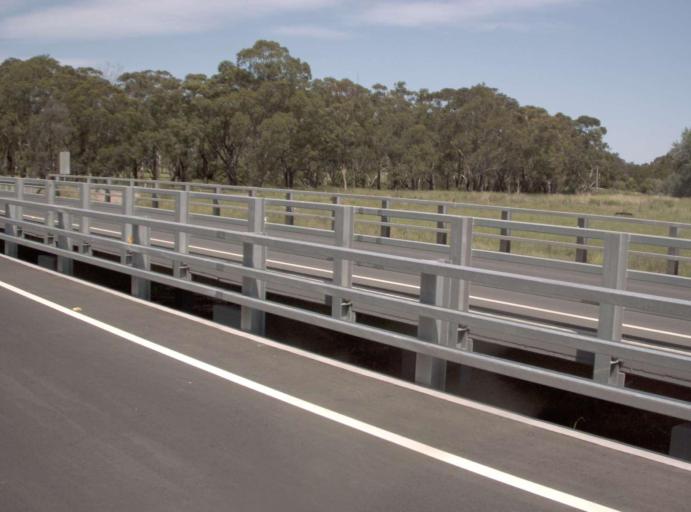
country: AU
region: Victoria
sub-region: Wellington
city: Sale
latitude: -38.1128
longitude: 147.0534
